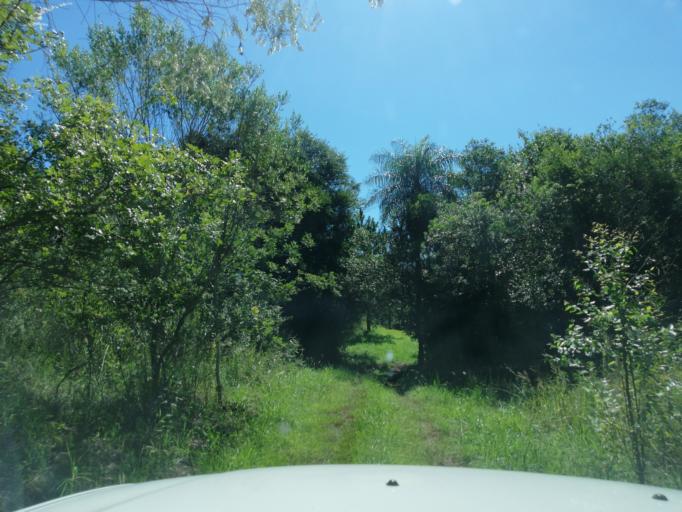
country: AR
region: Misiones
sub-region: Departamento de Leandro N. Alem
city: Leandro N. Alem
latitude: -27.5784
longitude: -55.3738
